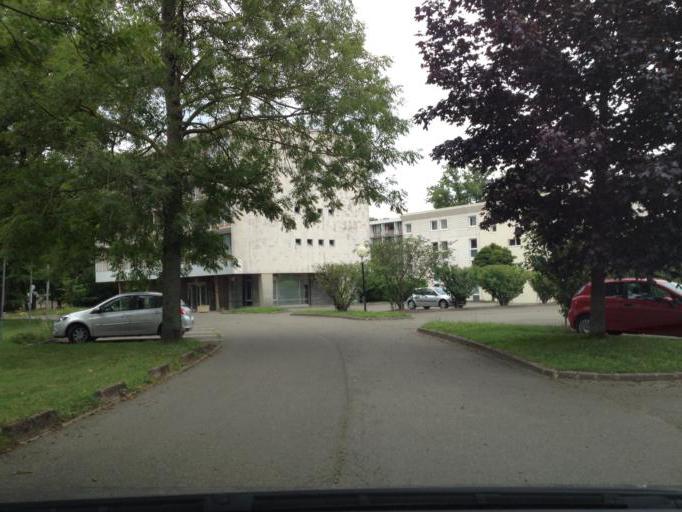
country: FR
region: Ile-de-France
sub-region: Departement des Yvelines
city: Jouy-en-Josas
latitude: 48.7568
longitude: 2.1682
